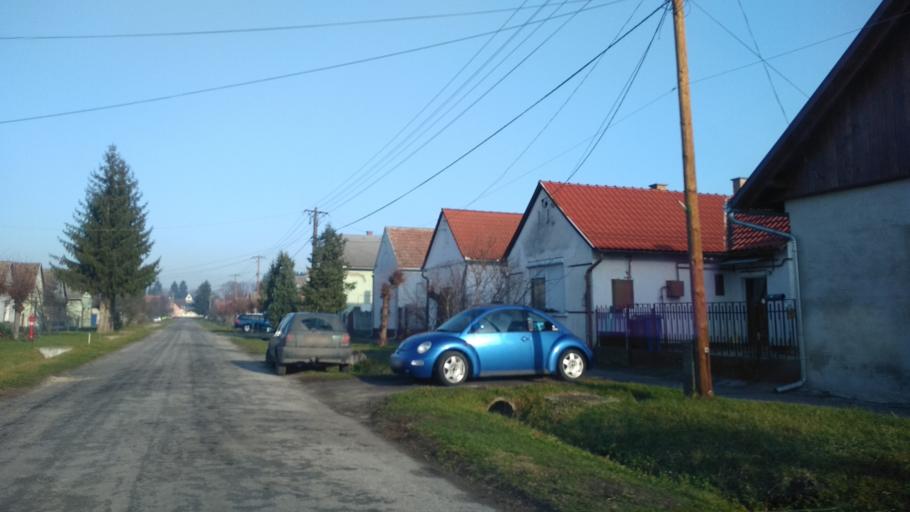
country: HU
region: Somogy
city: Barcs
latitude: 45.9633
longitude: 17.4746
